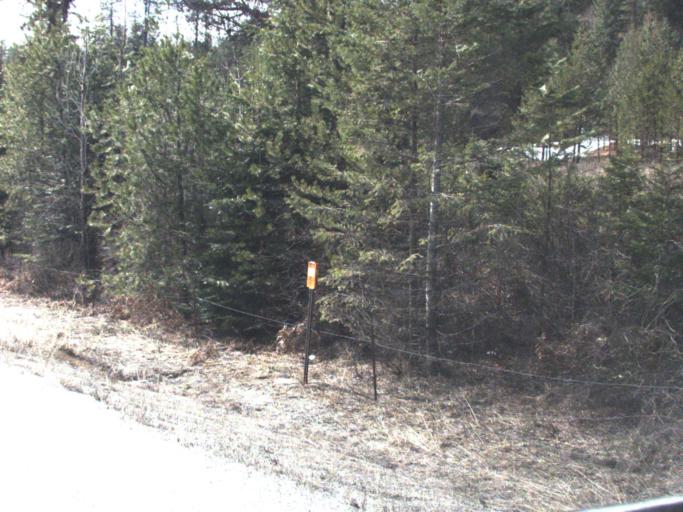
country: US
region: Washington
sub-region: Stevens County
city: Chewelah
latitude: 48.6286
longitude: -117.3685
